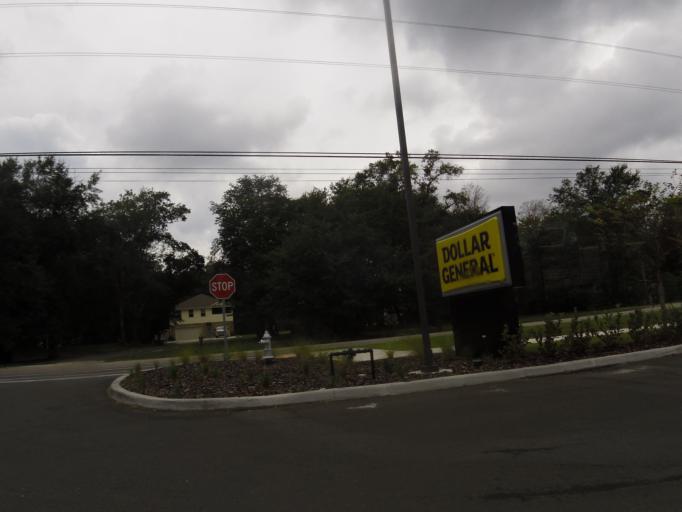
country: US
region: Florida
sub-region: Clay County
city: Middleburg
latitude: 30.1122
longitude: -81.8645
